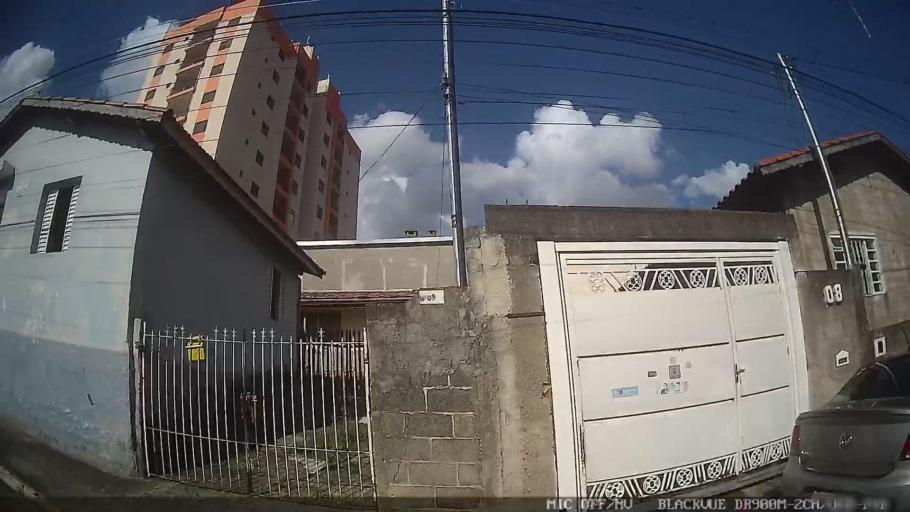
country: BR
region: Minas Gerais
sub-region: Extrema
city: Extrema
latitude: -22.8574
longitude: -46.3200
